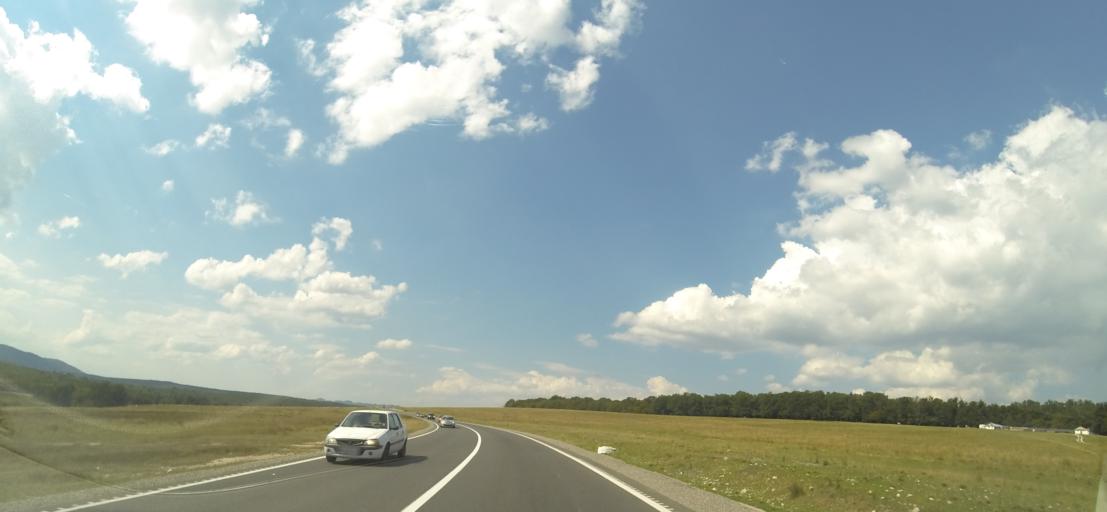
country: RO
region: Brasov
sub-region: Comuna Dumbravita
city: Dumbravita
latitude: 45.7479
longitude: 25.4121
